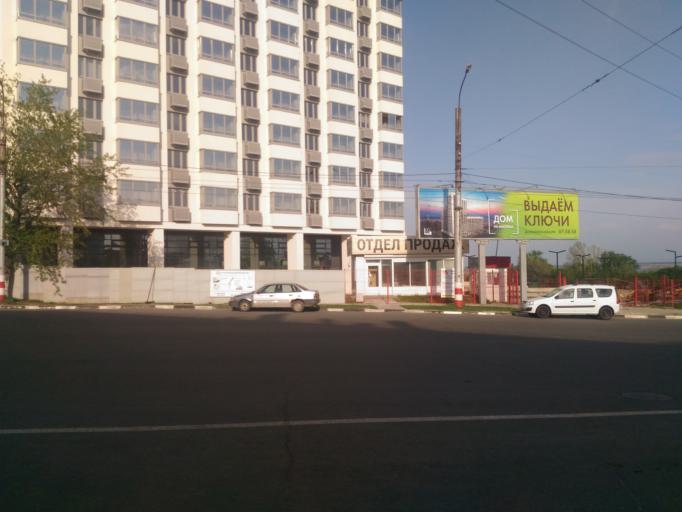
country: RU
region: Ulyanovsk
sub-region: Ulyanovskiy Rayon
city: Ulyanovsk
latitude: 54.3061
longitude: 48.3896
